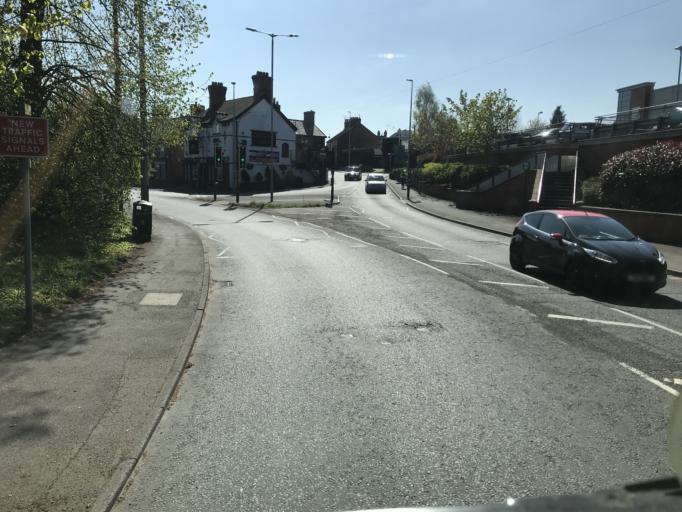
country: GB
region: England
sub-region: Cheshire East
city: Middlewich
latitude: 53.1944
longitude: -2.4539
